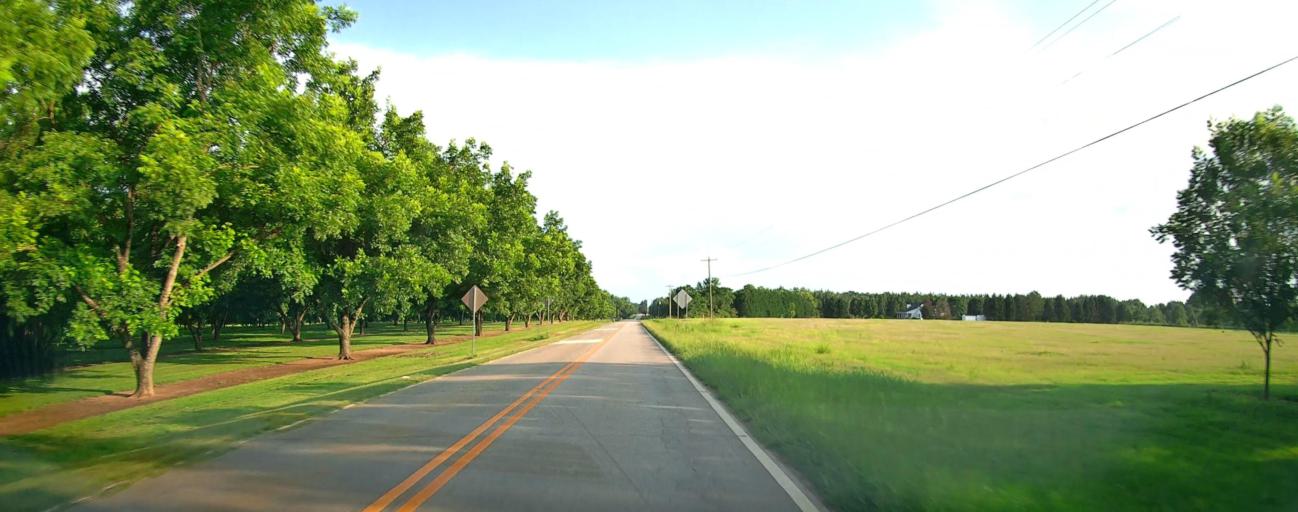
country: US
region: Georgia
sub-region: Peach County
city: Byron
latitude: 32.6724
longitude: -83.8609
